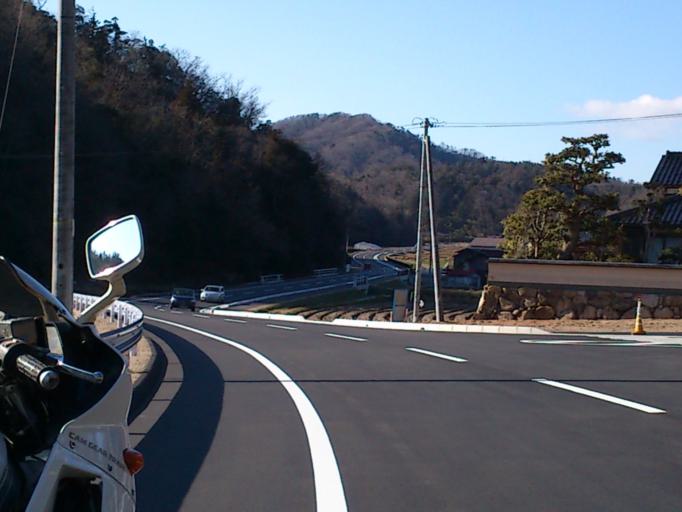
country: JP
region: Kyoto
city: Miyazu
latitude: 35.6090
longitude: 135.1357
